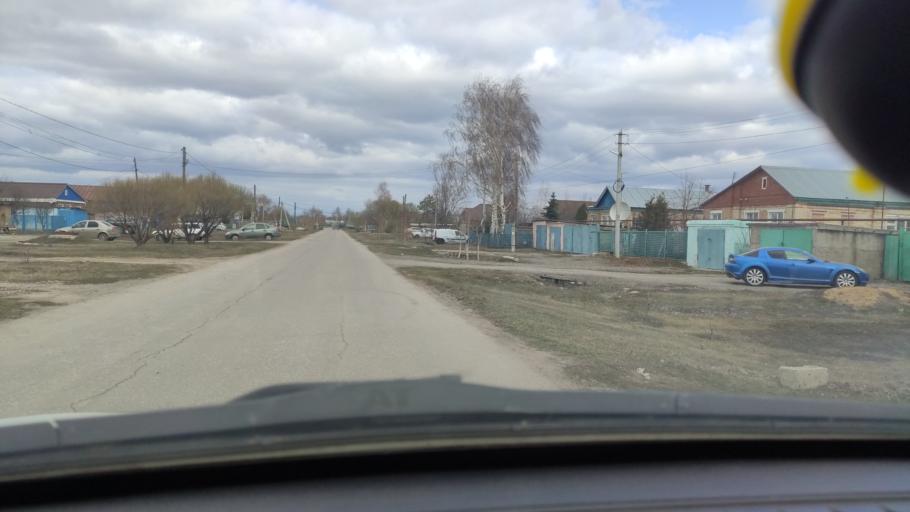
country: RU
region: Samara
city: Tol'yatti
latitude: 53.5645
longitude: 49.4002
